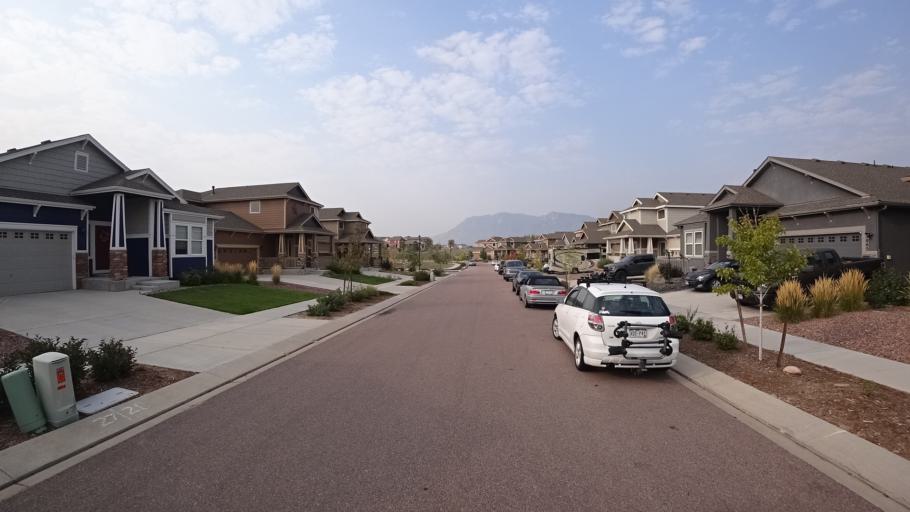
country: US
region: Colorado
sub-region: El Paso County
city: Stratmoor
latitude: 38.8138
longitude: -104.7856
